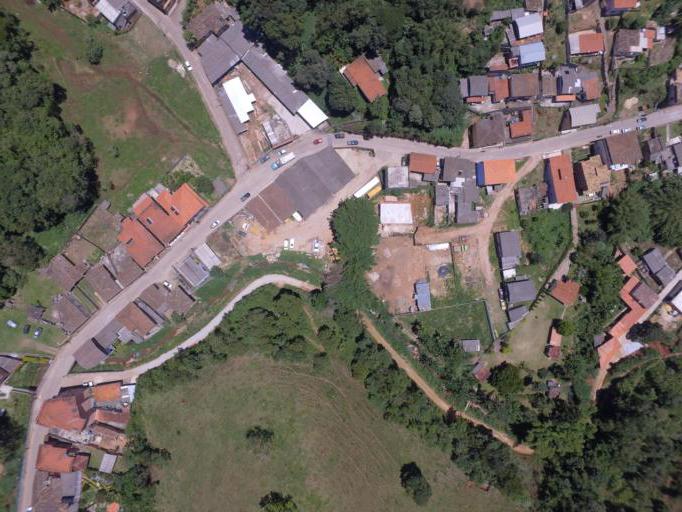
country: BR
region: Minas Gerais
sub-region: Tiradentes
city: Tiradentes
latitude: -21.0614
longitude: -44.0787
